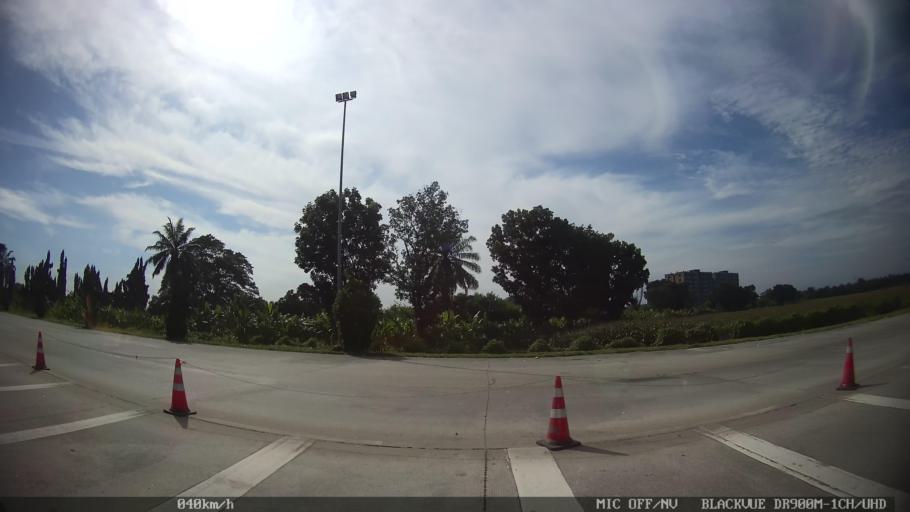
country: ID
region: North Sumatra
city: Sunggal
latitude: 3.6292
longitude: 98.6316
